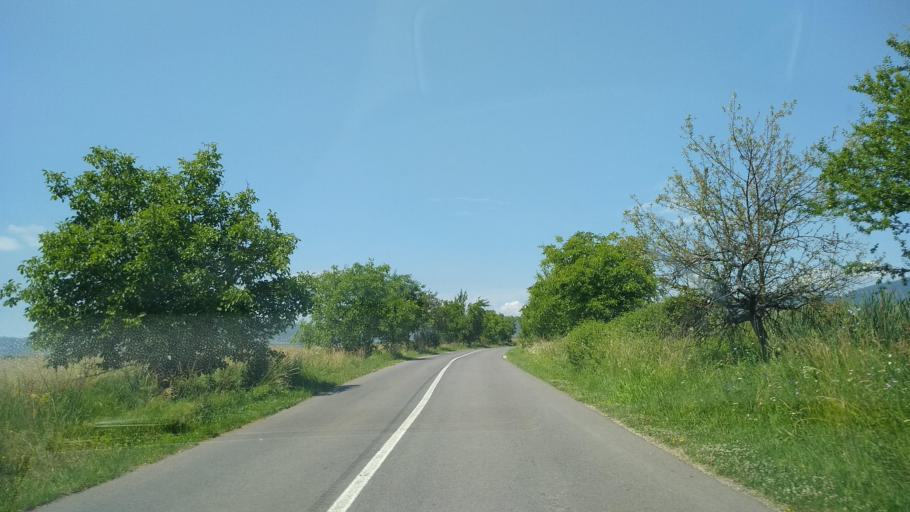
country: RO
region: Hunedoara
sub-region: Comuna Totesti
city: Totesti
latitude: 45.5728
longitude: 22.8710
